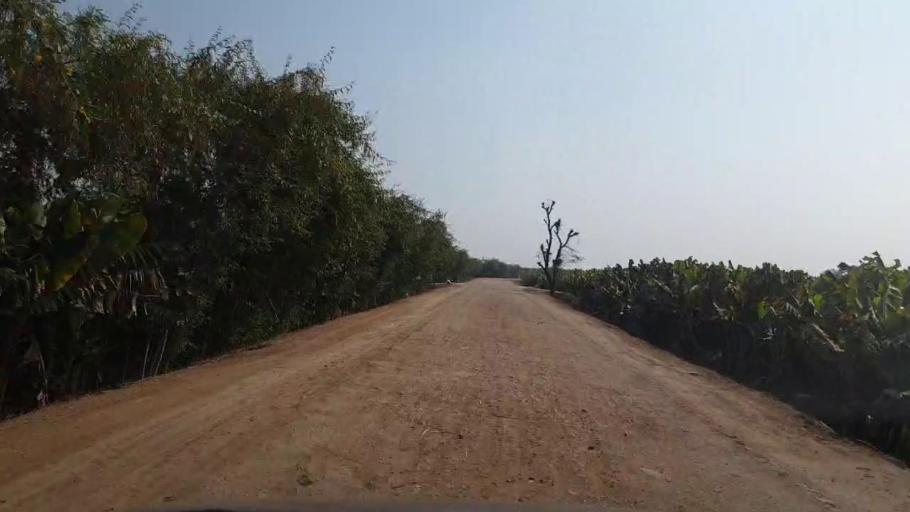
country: PK
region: Sindh
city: Bhit Shah
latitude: 25.7915
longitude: 68.4963
